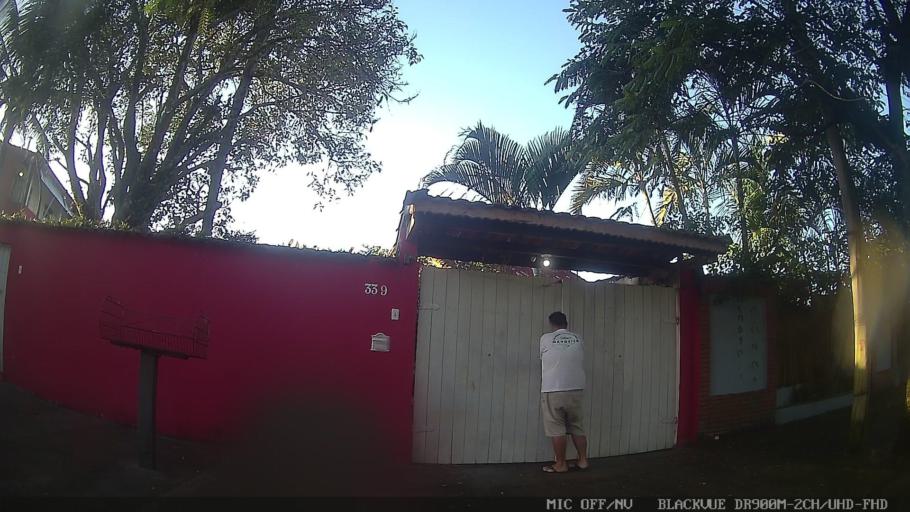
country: BR
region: Sao Paulo
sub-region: Itanhaem
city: Itanhaem
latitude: -24.2337
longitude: -46.8789
